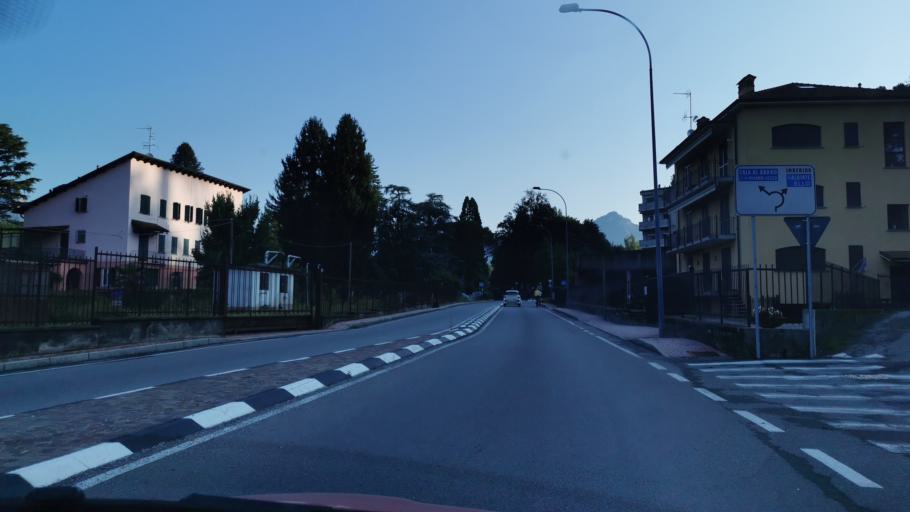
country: IT
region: Lombardy
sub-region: Provincia di Lecco
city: Oggiono
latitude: 45.7923
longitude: 9.3526
